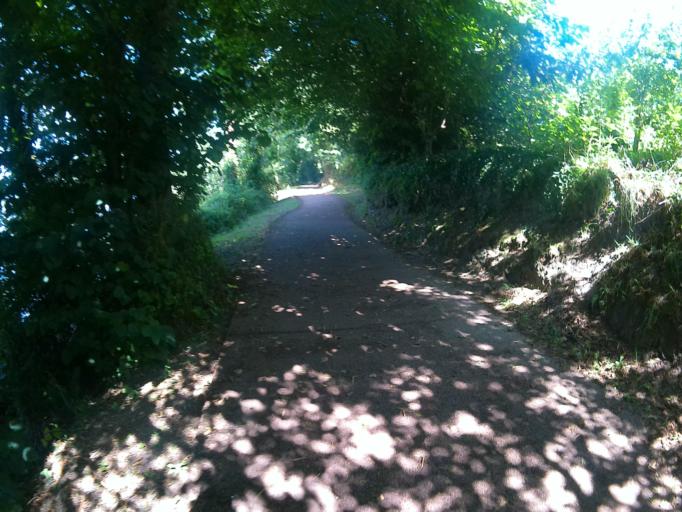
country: PT
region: Viana do Castelo
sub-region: Valenca
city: Valenca
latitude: 41.9995
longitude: -8.6655
